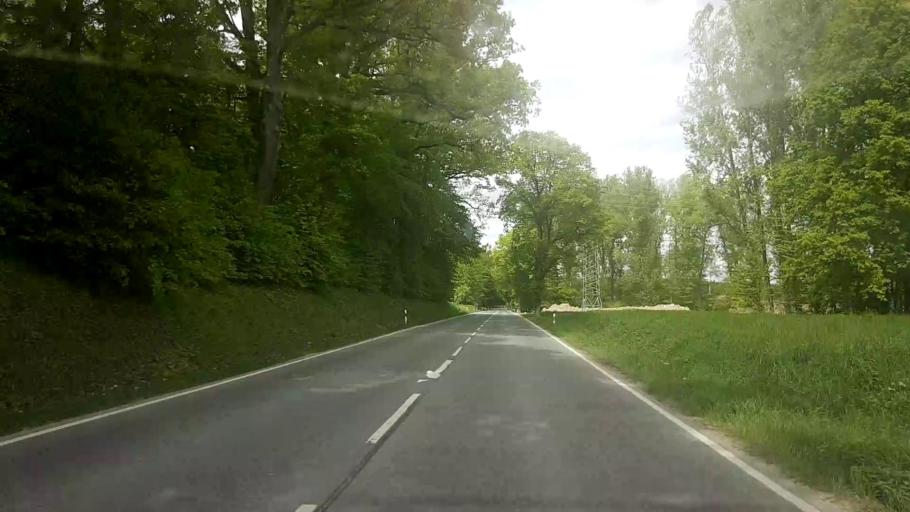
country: DE
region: Bavaria
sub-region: Upper Franconia
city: Lichtenfels
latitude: 50.1598
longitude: 11.0581
